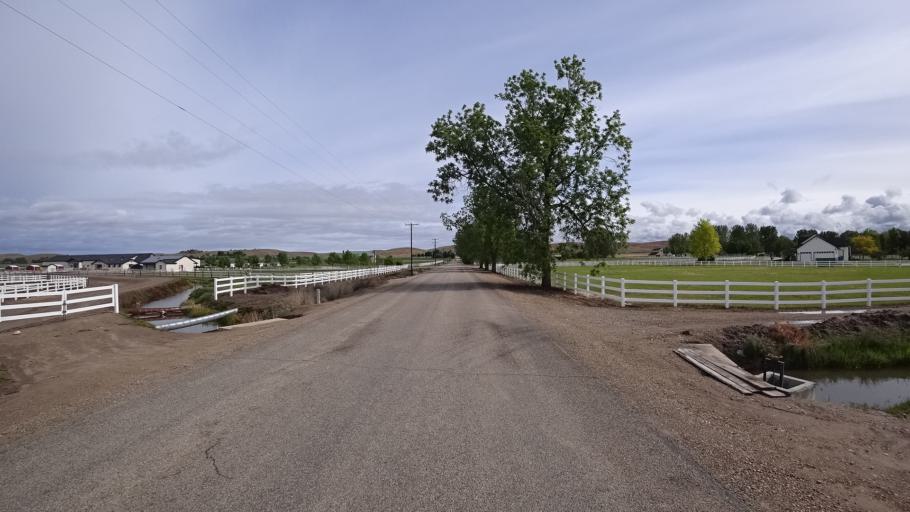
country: US
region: Idaho
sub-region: Ada County
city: Eagle
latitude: 43.7283
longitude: -116.4134
